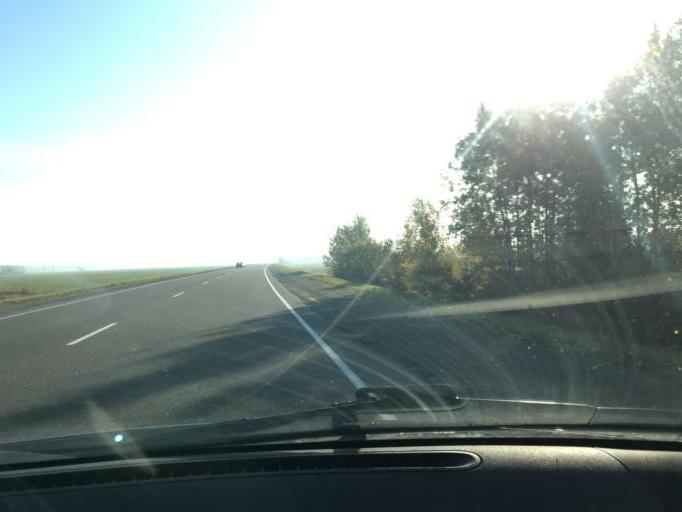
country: BY
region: Brest
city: Horad Luninyets
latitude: 52.3160
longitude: 26.6370
